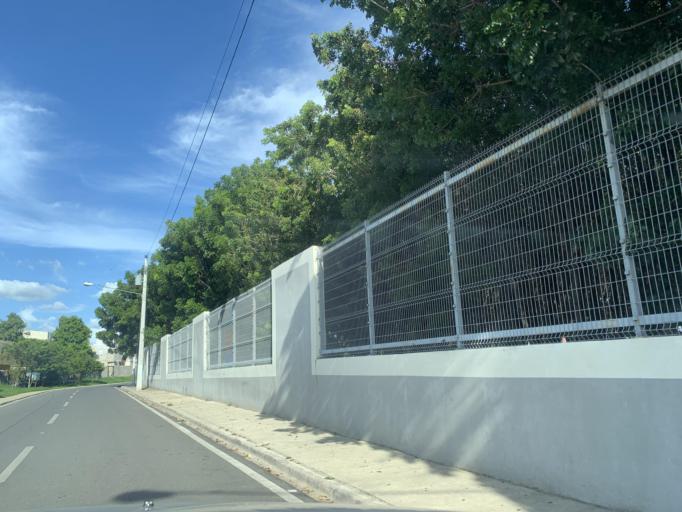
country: DO
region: Santiago
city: Santiago de los Caballeros
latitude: 19.4714
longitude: -70.7033
